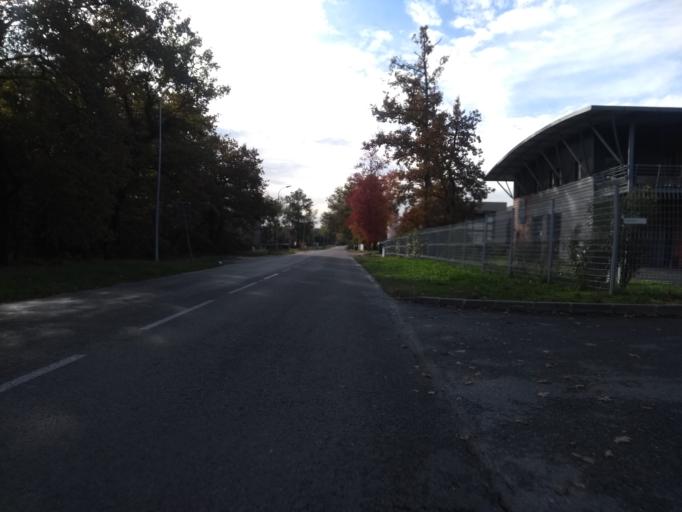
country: FR
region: Aquitaine
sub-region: Departement de la Gironde
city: Cestas
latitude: 44.7634
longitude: -0.6695
